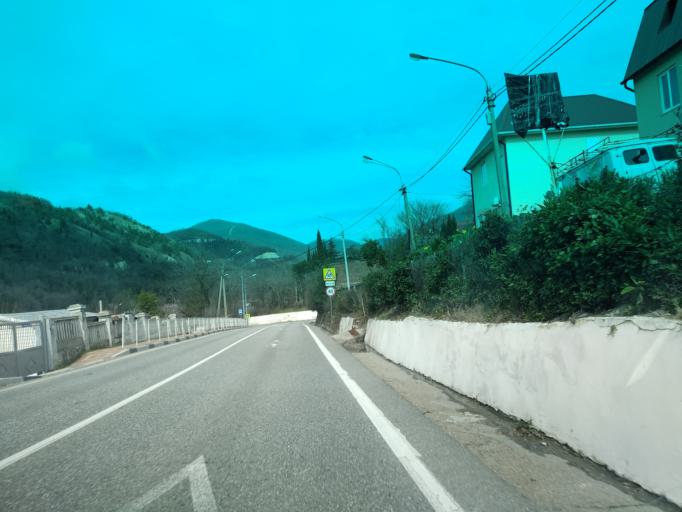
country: RU
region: Krasnodarskiy
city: Shepsi
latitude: 44.0568
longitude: 39.1347
